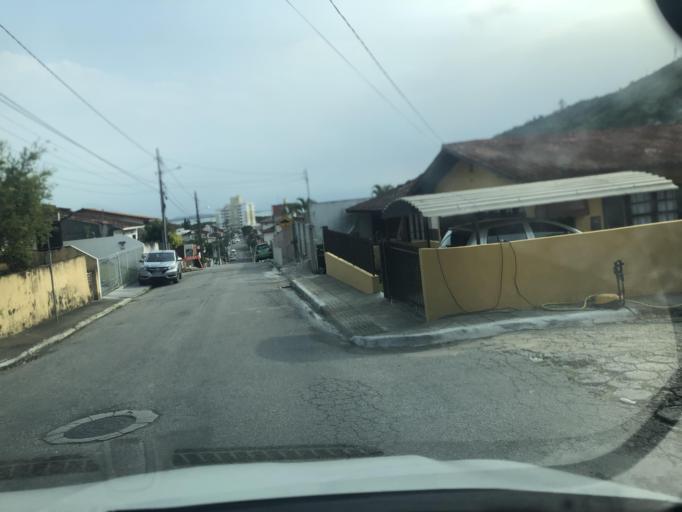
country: BR
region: Santa Catarina
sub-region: Florianopolis
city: Saco dos Limoes
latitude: -27.6040
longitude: -48.5350
